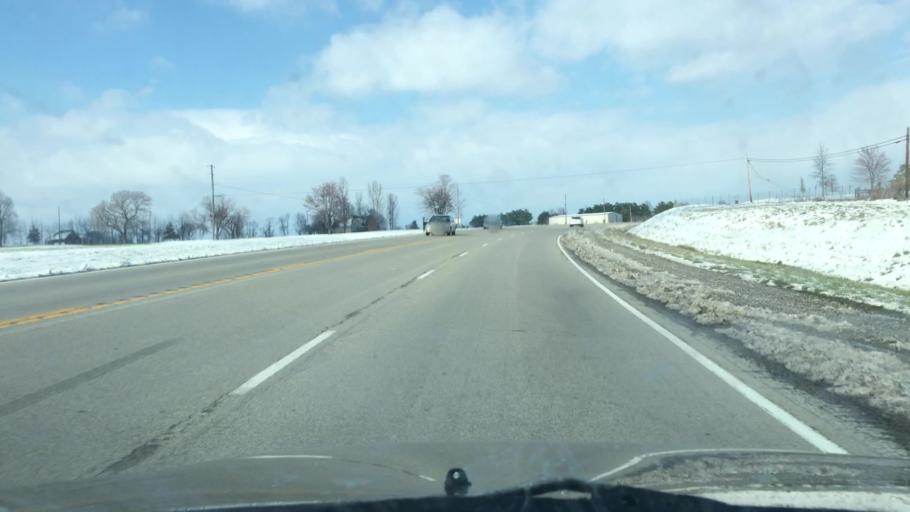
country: US
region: Kentucky
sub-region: Marion County
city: Lebanon
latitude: 37.5446
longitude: -85.3038
